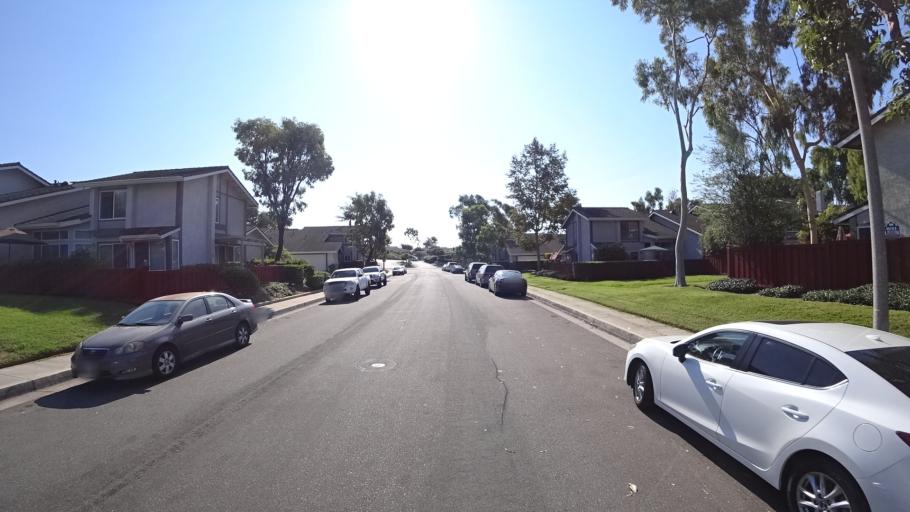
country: US
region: California
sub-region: Orange County
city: Dana Point
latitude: 33.4512
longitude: -117.6531
